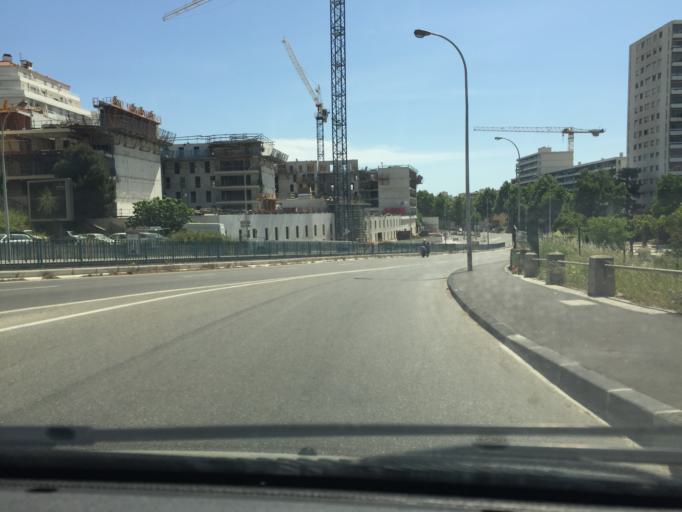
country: FR
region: Provence-Alpes-Cote d'Azur
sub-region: Departement des Bouches-du-Rhone
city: Marseille 13
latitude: 43.3133
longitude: 5.4051
